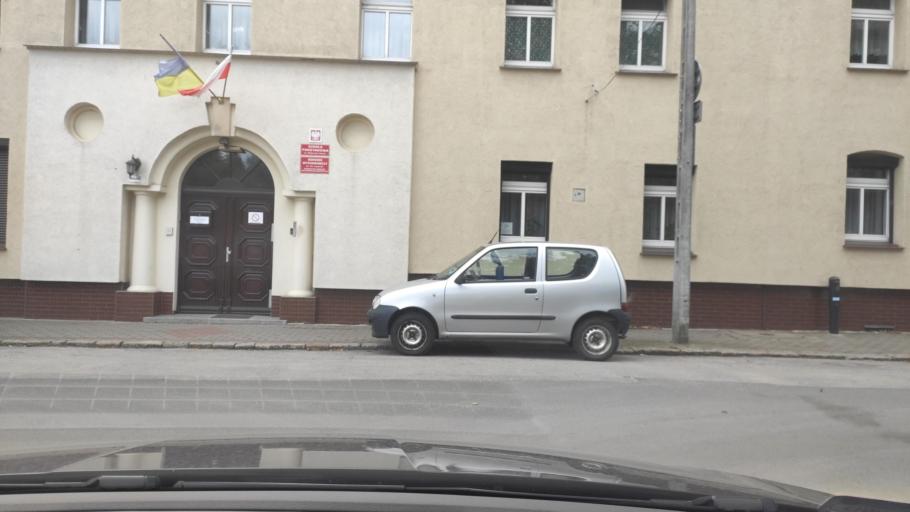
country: PL
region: Greater Poland Voivodeship
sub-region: Powiat poznanski
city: Czerwonak
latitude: 52.4231
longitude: 16.9703
